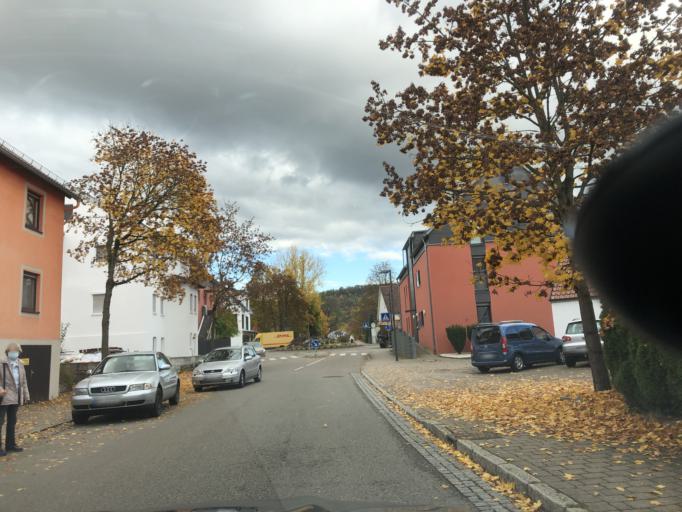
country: DE
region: Baden-Wuerttemberg
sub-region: Regierungsbezirk Stuttgart
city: Winterbach
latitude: 48.8013
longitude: 9.4788
